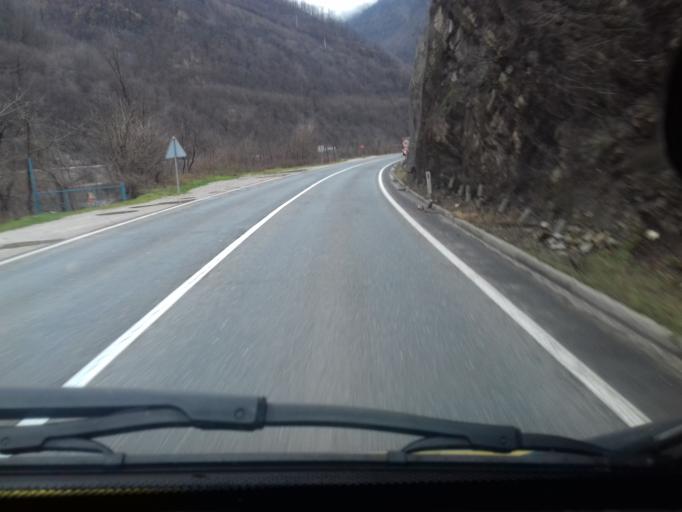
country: BA
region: Federation of Bosnia and Herzegovina
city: Zeljezno Polje
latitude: 44.3088
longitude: 17.9049
